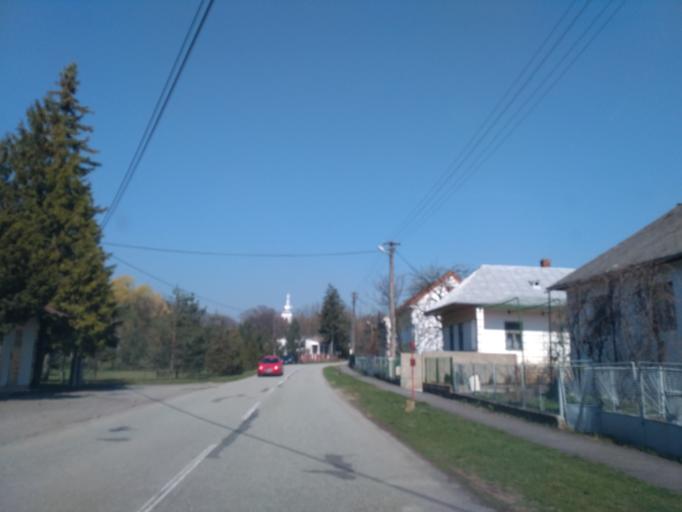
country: SK
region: Kosicky
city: Secovce
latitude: 48.7634
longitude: 21.6592
